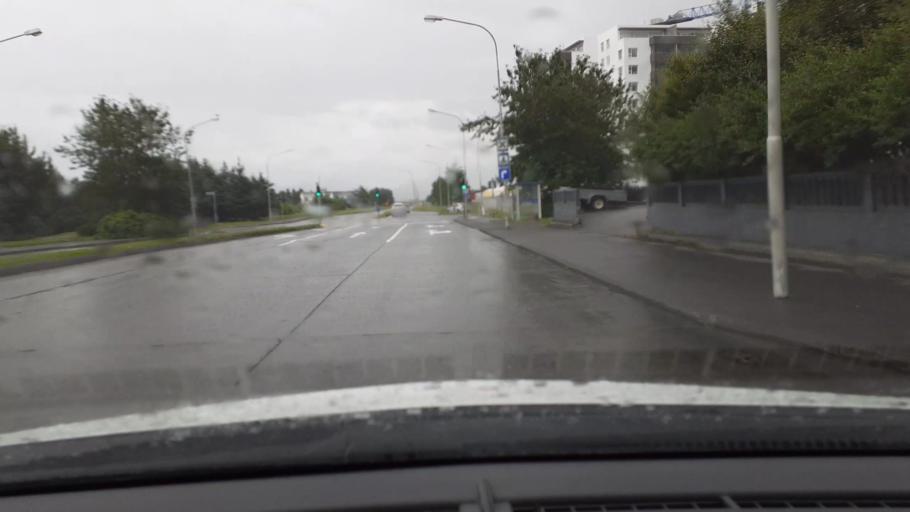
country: IS
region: West
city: Akranes
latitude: 64.3211
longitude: -22.0757
